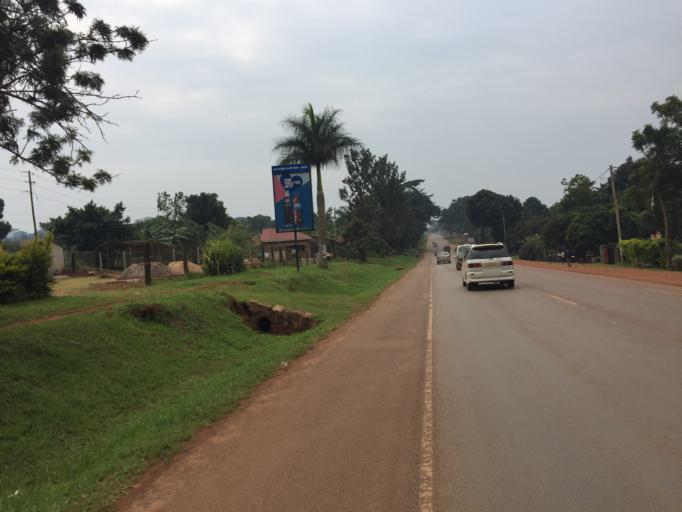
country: UG
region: Central Region
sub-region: Wakiso District
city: Kajansi
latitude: 0.1324
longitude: 32.5344
